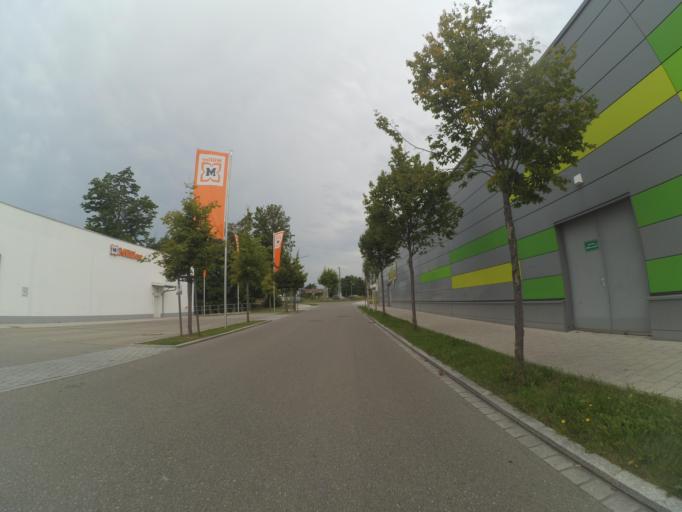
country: DE
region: Bavaria
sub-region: Swabia
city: Buchloe
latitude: 48.0355
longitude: 10.7192
